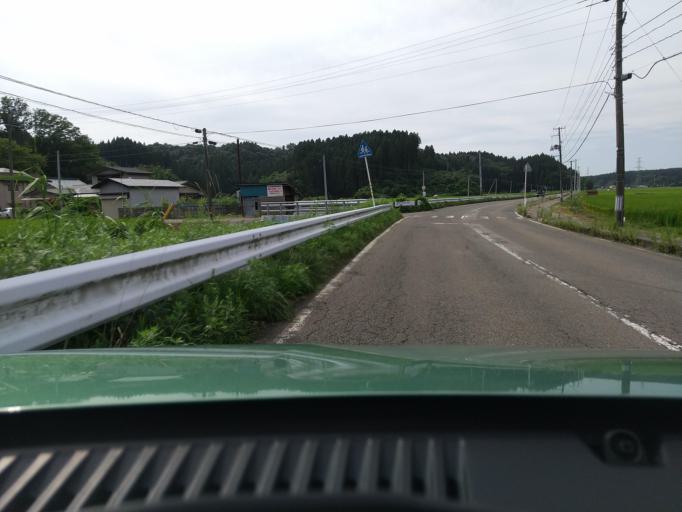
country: JP
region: Akita
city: Akita
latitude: 39.7841
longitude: 140.1259
